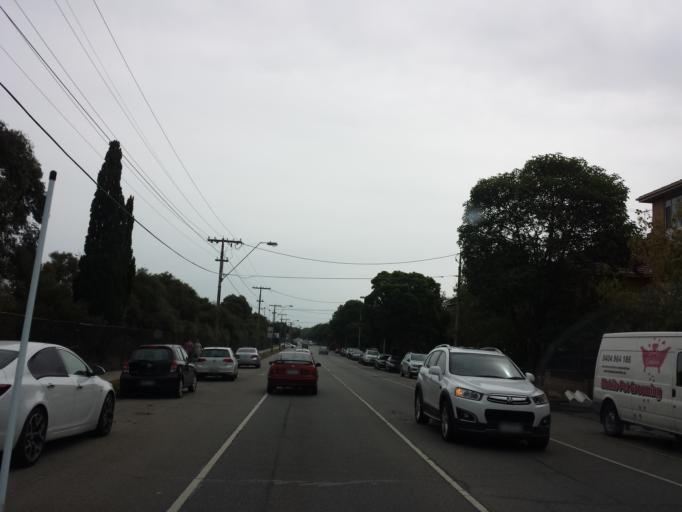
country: AU
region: Victoria
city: Ripponlea
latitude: -37.8837
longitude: 144.9954
